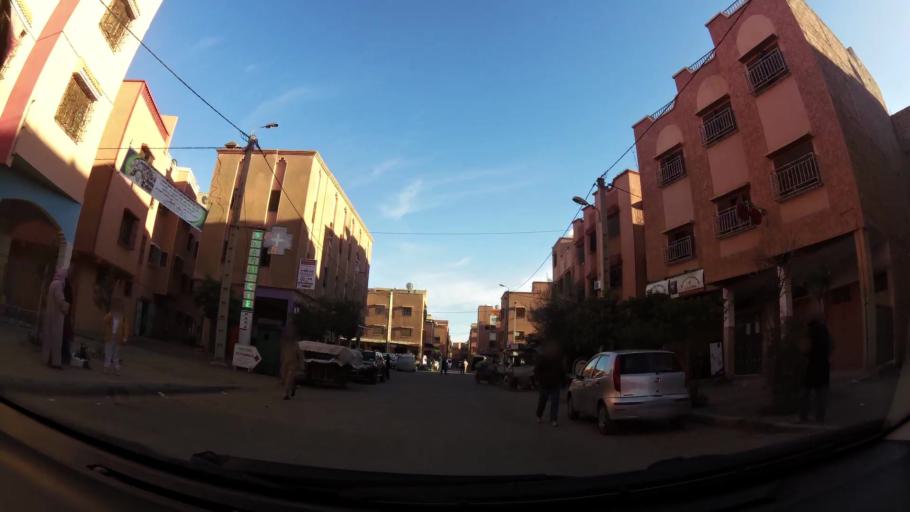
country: MA
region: Marrakech-Tensift-Al Haouz
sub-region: Marrakech
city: Marrakesh
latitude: 31.6180
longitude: -8.0485
